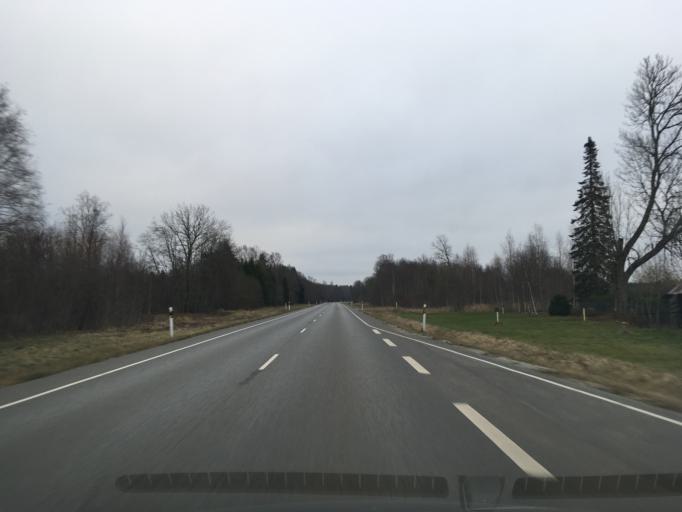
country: EE
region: Laeaene-Virumaa
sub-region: Kadrina vald
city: Kadrina
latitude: 59.4504
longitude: 26.0465
